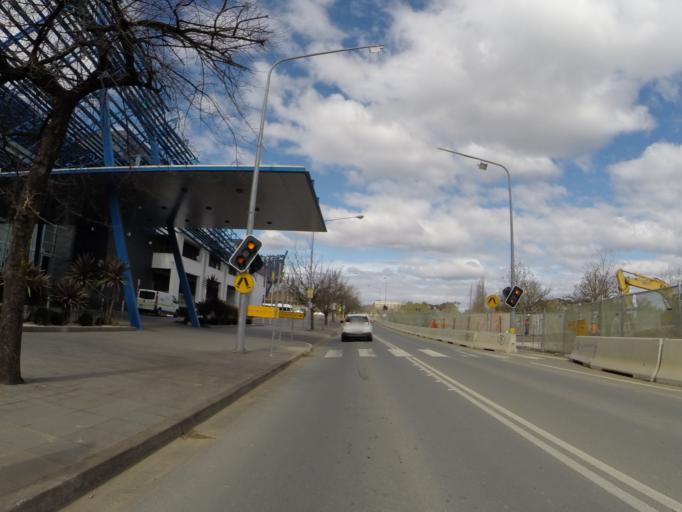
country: AU
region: Australian Capital Territory
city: Canberra
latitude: -35.2849
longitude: 149.1339
